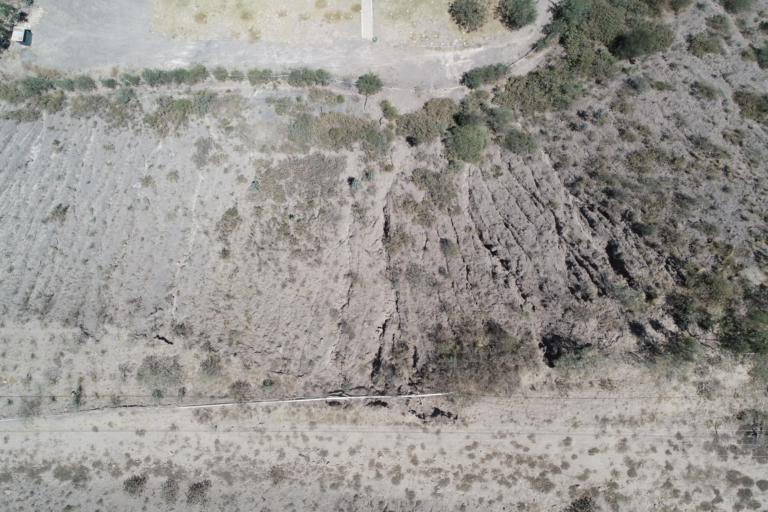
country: BO
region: La Paz
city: La Paz
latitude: -16.6130
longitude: -68.0612
